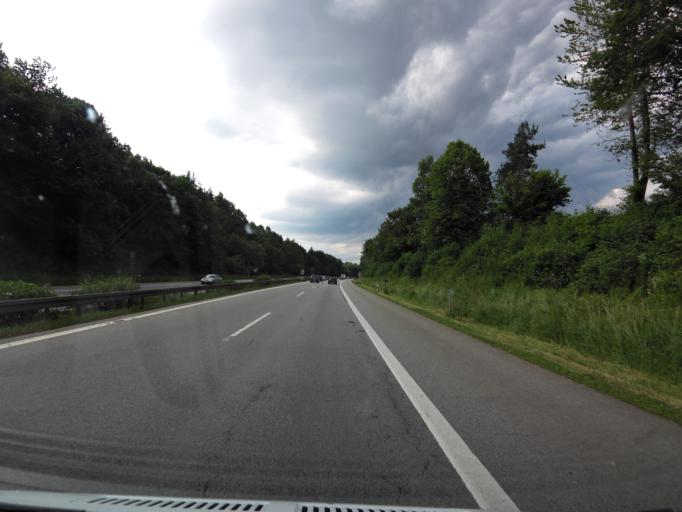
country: DE
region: Bavaria
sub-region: Lower Bavaria
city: Aussernzell
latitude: 48.6903
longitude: 13.2003
